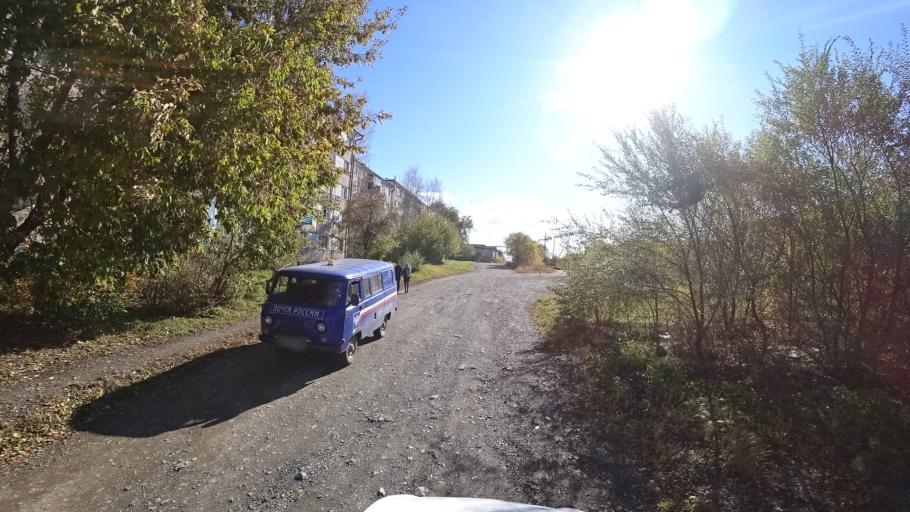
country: RU
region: Khabarovsk Krai
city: Amursk
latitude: 50.2213
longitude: 136.9012
